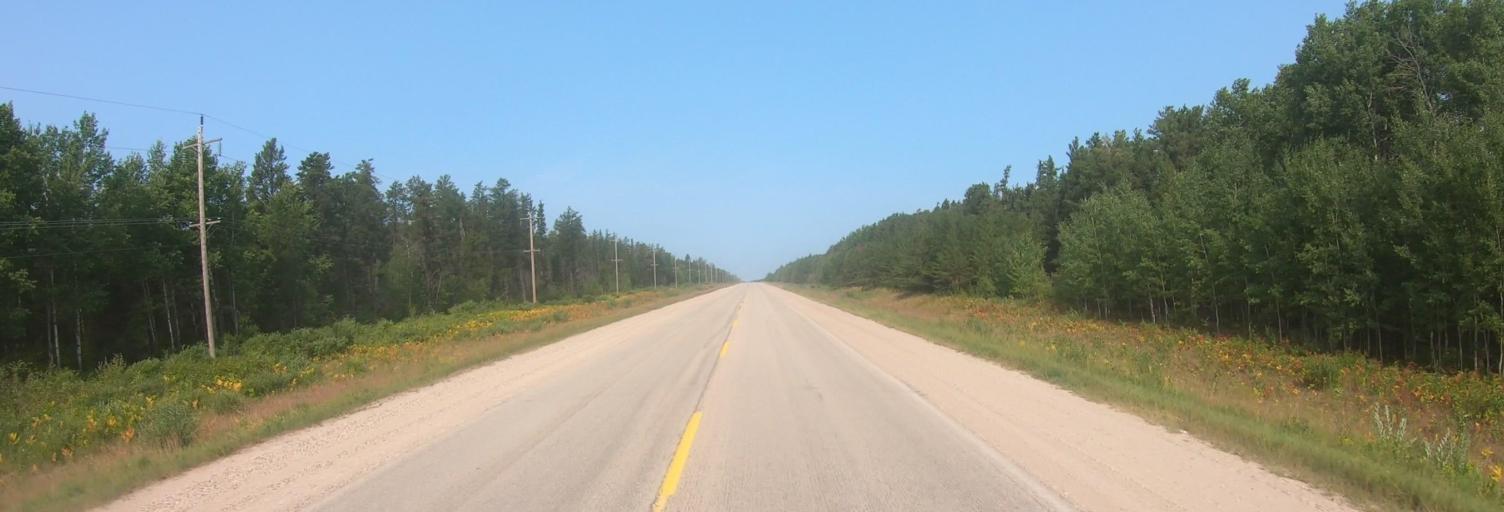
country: US
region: Minnesota
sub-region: Roseau County
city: Roseau
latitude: 49.0762
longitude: -95.8599
